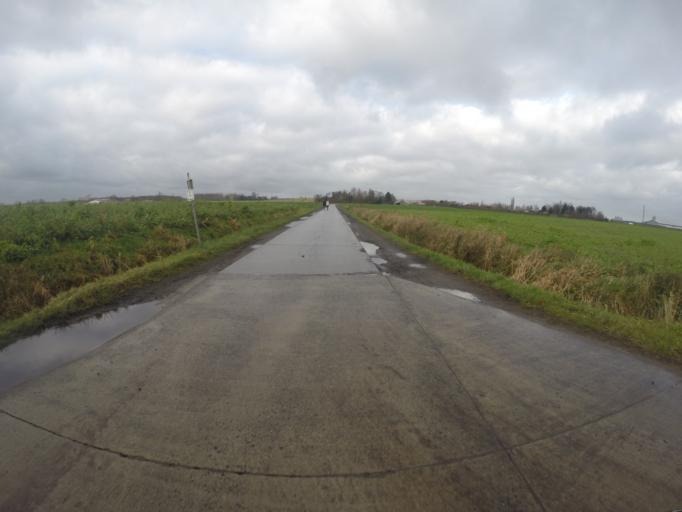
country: BE
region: Flanders
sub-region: Provincie Oost-Vlaanderen
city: Zomergem
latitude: 51.1469
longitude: 3.5159
